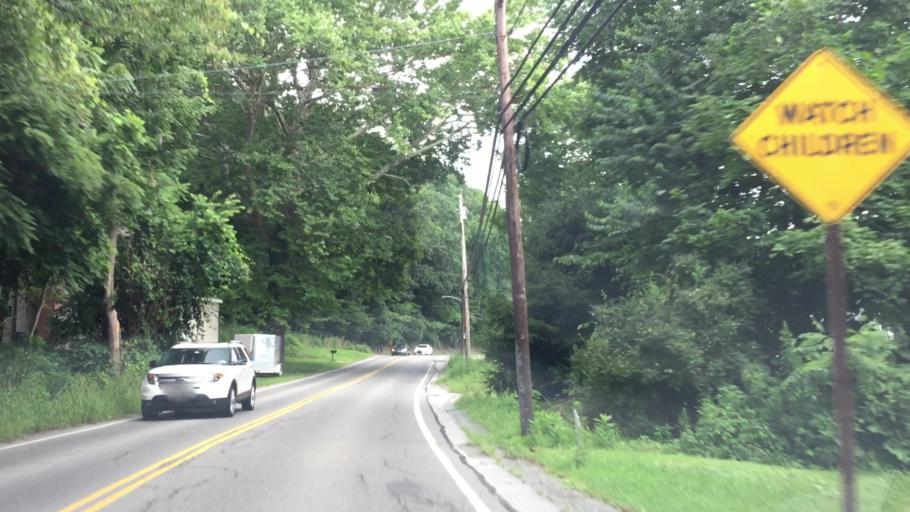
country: US
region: Pennsylvania
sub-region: Allegheny County
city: Enlow
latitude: 40.4522
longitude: -80.2030
